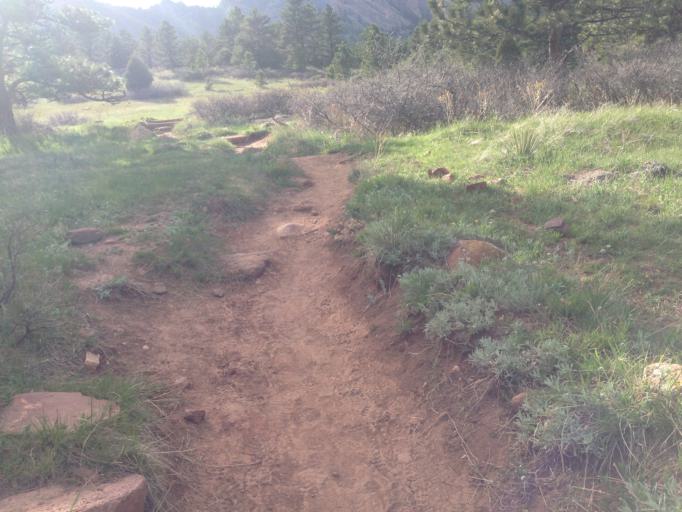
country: US
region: Colorado
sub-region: Boulder County
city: Boulder
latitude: 39.9427
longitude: -105.2724
